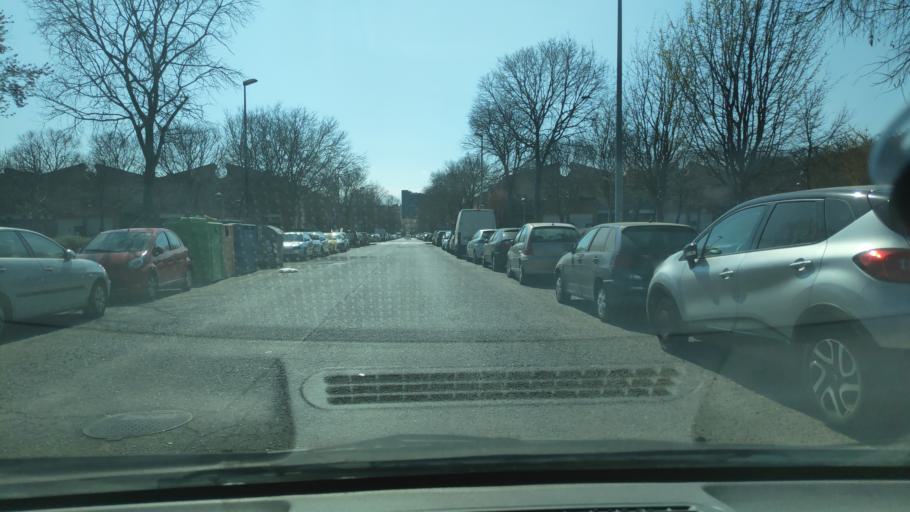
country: ES
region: Catalonia
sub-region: Provincia de Barcelona
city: Mollet del Valles
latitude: 41.5401
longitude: 2.2203
